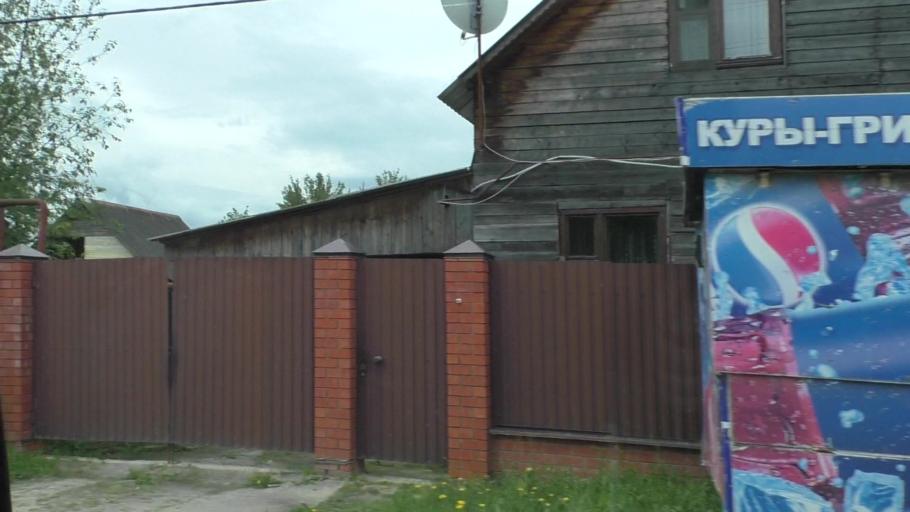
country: RU
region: Moskovskaya
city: Il'inskiy Pogost
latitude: 55.4711
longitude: 38.8954
